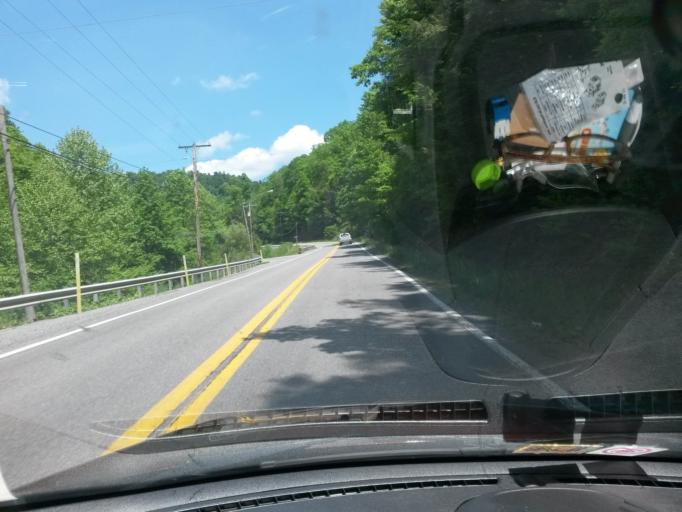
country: US
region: West Virginia
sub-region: McDowell County
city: Welch
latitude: 37.4760
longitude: -81.5437
